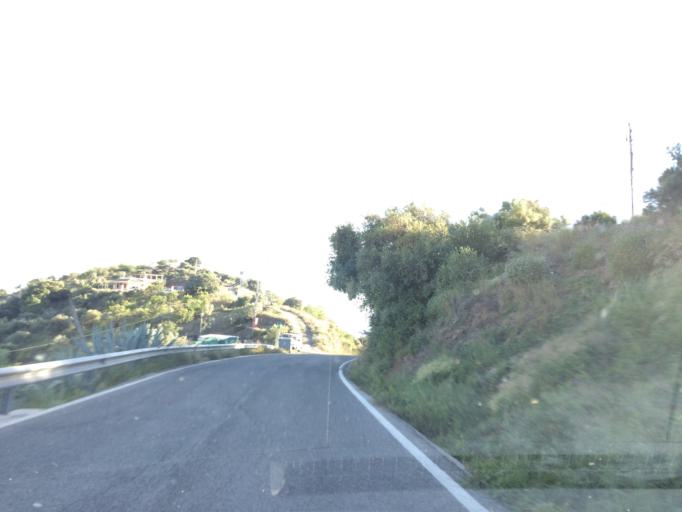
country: ES
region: Andalusia
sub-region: Provincia de Malaga
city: Totalan
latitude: 36.7549
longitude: -4.3300
